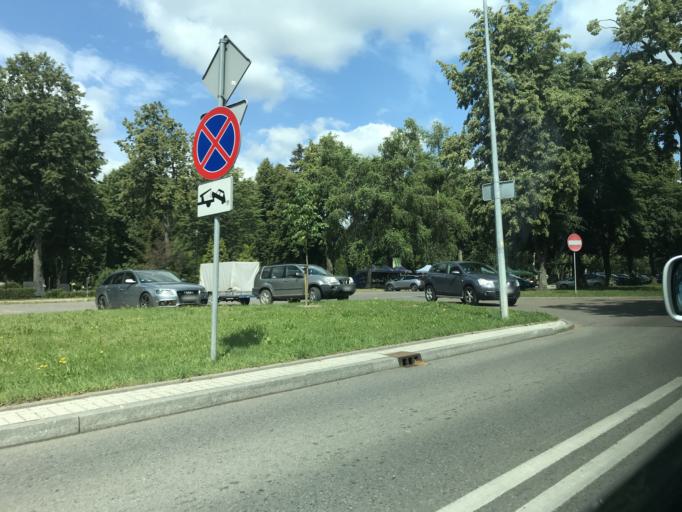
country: PL
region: Warmian-Masurian Voivodeship
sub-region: Powiat elblaski
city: Elblag
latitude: 54.1681
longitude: 19.4244
